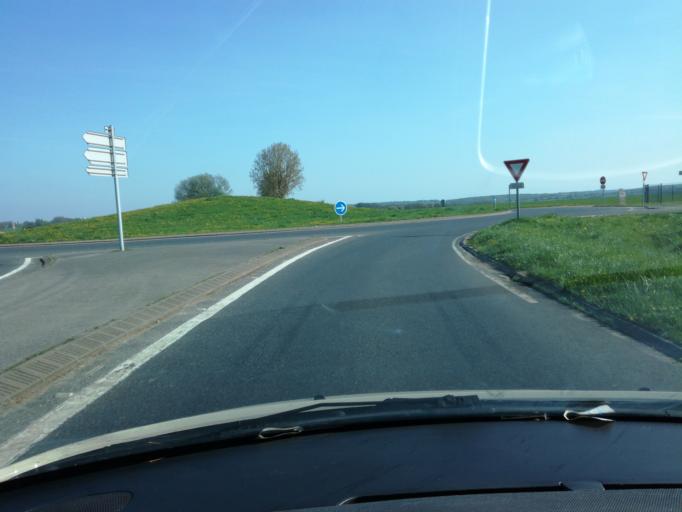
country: FR
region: Picardie
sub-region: Departement de la Somme
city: Poix-de-Picardie
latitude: 49.8081
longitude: 1.9664
